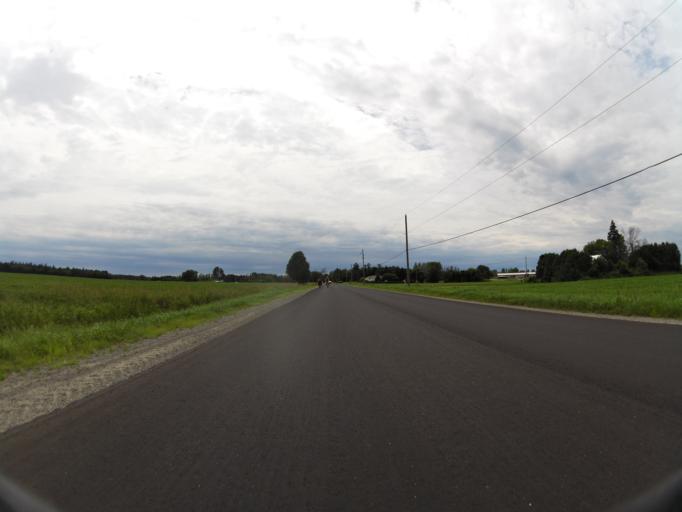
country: CA
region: Ontario
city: Bells Corners
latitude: 45.0628
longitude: -75.6067
